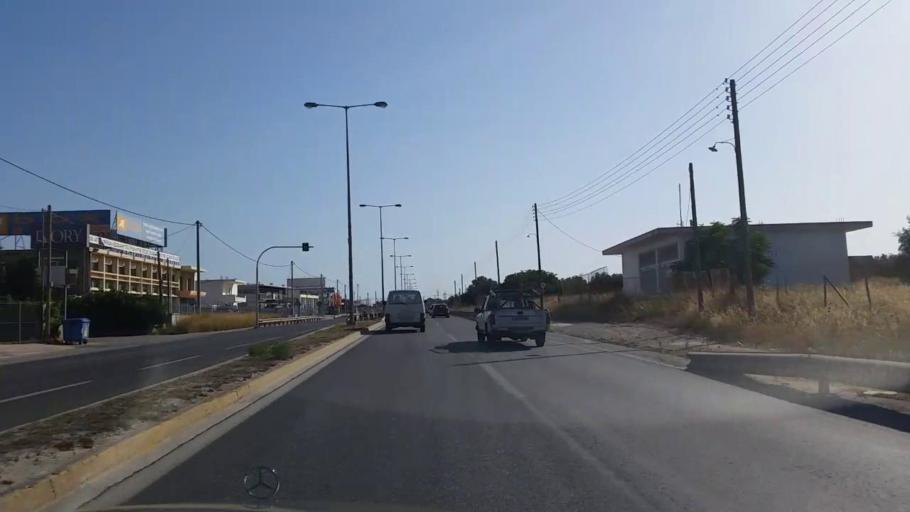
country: GR
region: Attica
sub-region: Nomarchia Anatolikis Attikis
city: Kitsi
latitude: 37.8707
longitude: 23.8571
